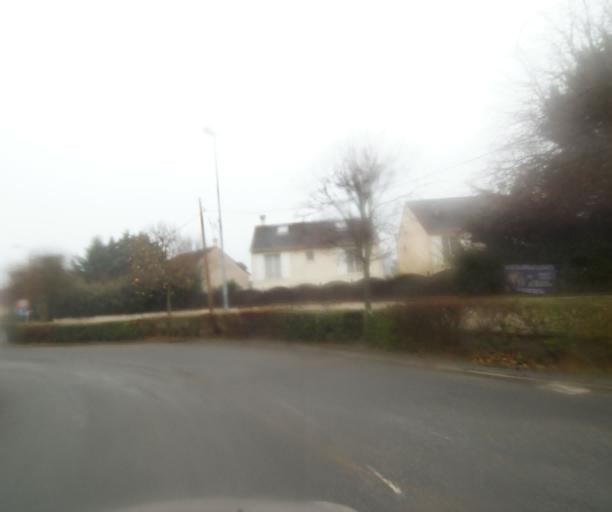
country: FR
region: Ile-de-France
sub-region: Departement de Seine-Saint-Denis
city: Coubron
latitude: 48.9157
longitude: 2.5927
